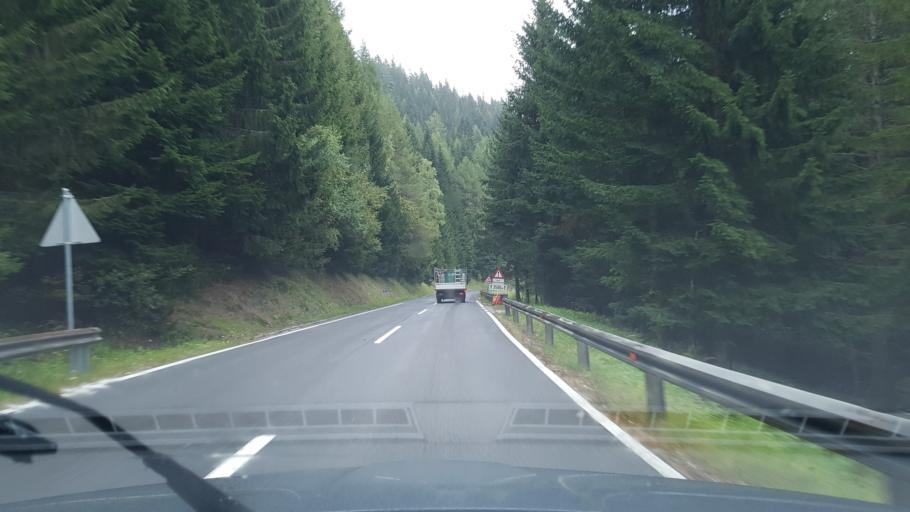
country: AT
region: Styria
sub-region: Politischer Bezirk Voitsberg
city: Salla
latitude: 47.1123
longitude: 14.9282
